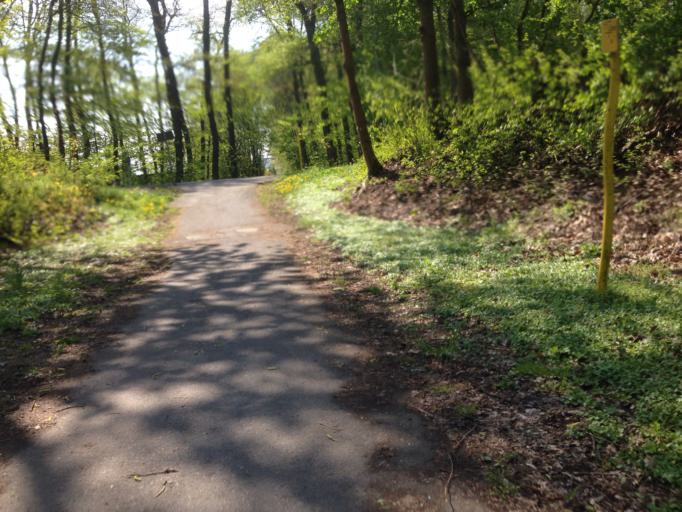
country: DE
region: Hesse
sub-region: Regierungsbezirk Giessen
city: Giessen
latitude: 50.5944
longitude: 8.7013
